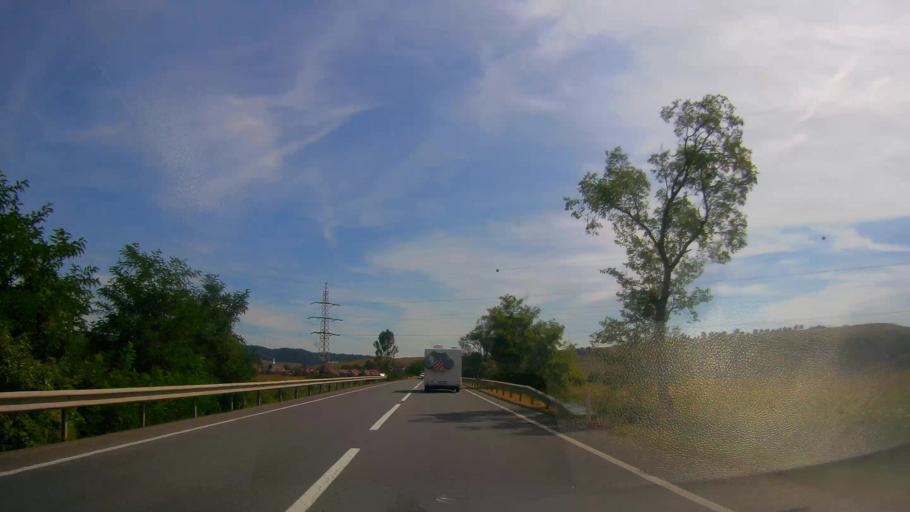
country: RO
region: Mures
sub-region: Comuna Balauseri
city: Chendu
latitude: 46.3983
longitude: 24.7105
